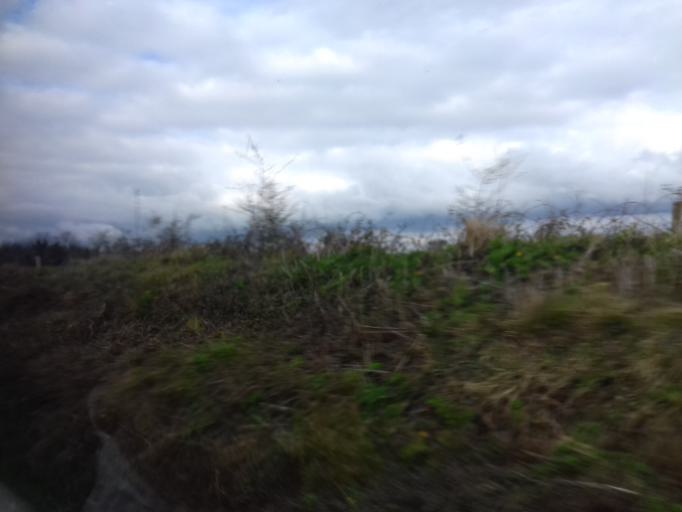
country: IE
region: Leinster
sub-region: An Iarmhi
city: An Muileann gCearr
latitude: 53.6341
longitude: -7.4187
